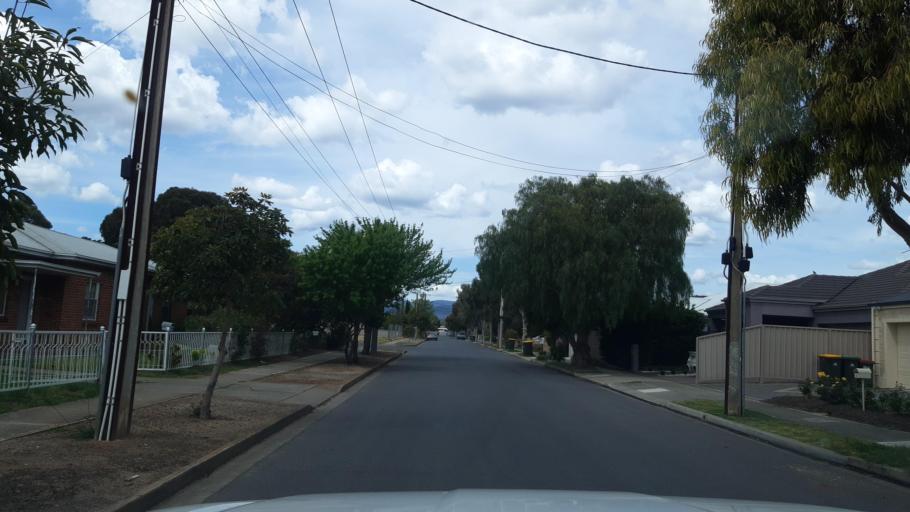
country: AU
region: South Australia
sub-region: Marion
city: Plympton Park
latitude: -34.9826
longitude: 138.5507
